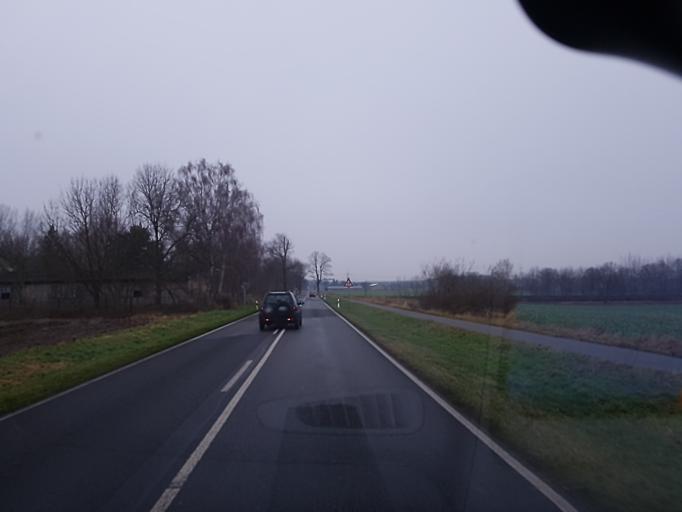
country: DE
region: Brandenburg
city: Lubbenau
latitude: 51.8750
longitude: 13.9121
